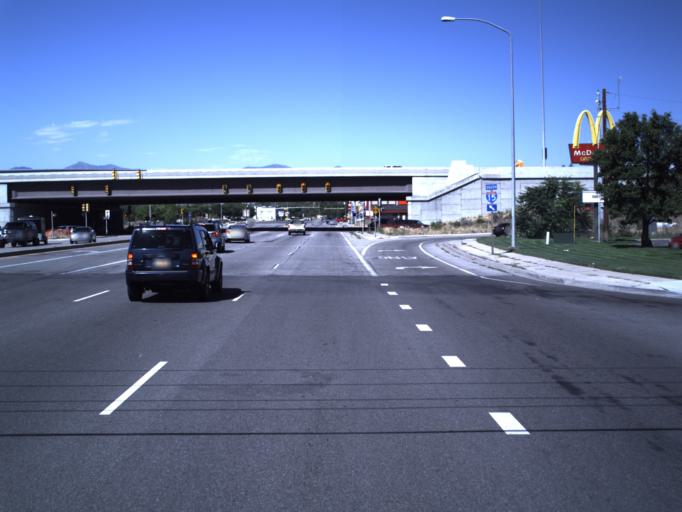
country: US
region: Utah
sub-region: Salt Lake County
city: Murray
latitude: 40.6746
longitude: -111.8996
